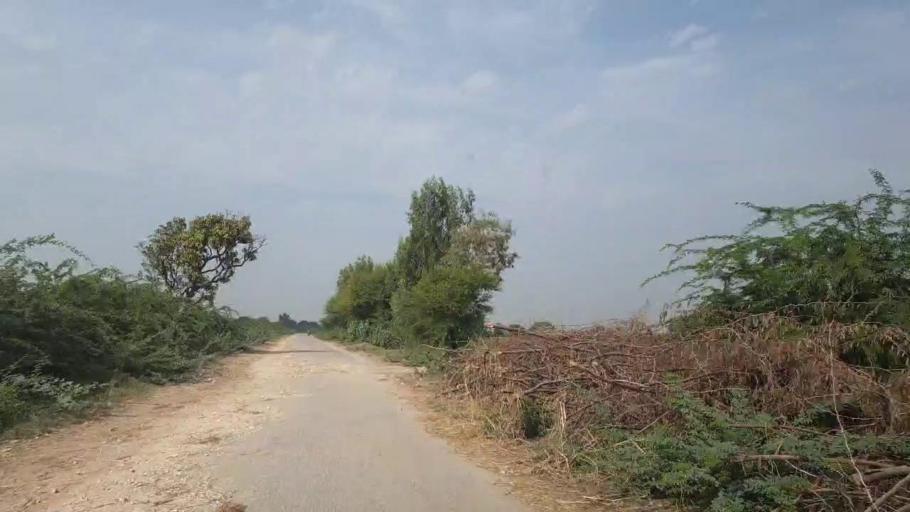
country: PK
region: Sindh
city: Tando Bago
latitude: 24.9243
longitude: 68.9910
